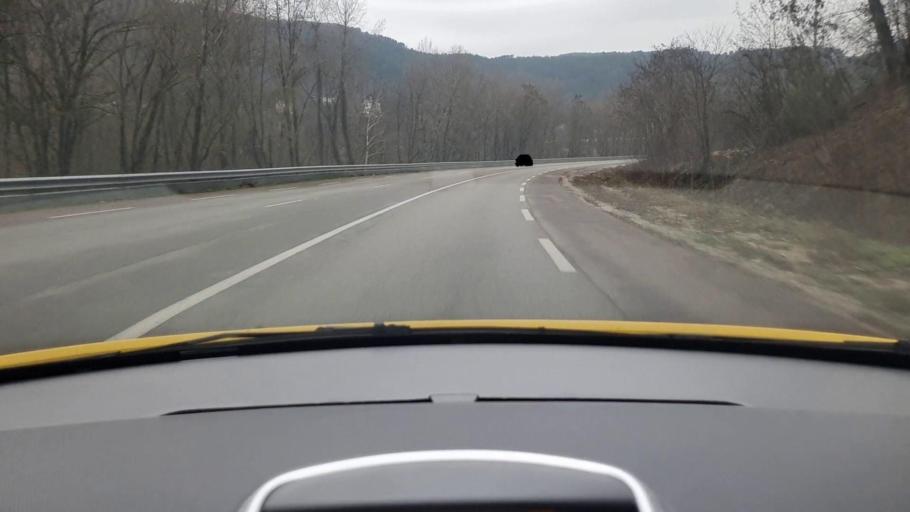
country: FR
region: Languedoc-Roussillon
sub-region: Departement du Gard
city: Molieres-sur-Ceze
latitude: 44.2638
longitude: 4.1638
